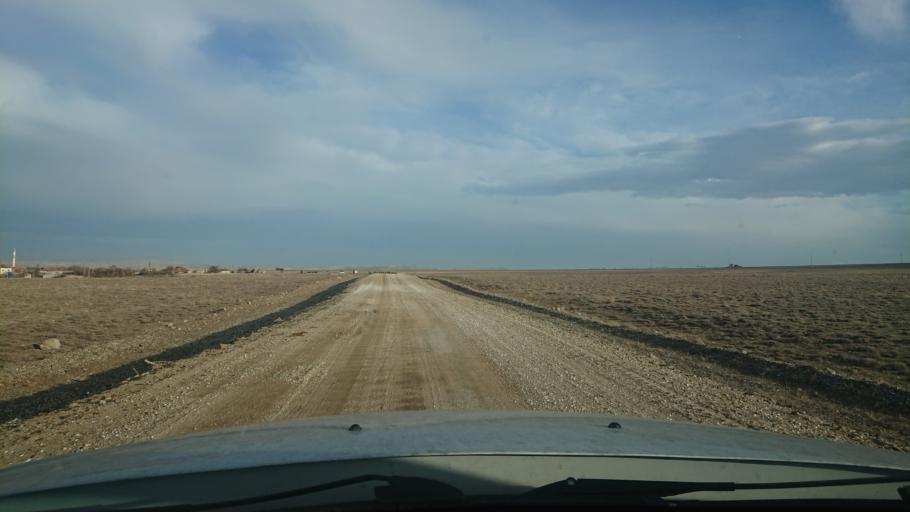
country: TR
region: Aksaray
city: Agacoren
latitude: 38.7108
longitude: 33.8685
